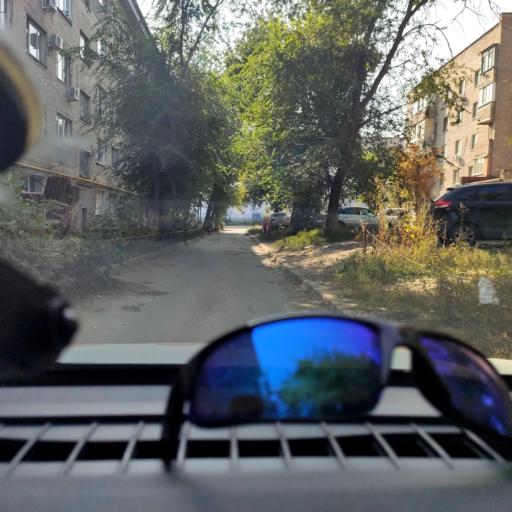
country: RU
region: Samara
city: Samara
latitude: 53.1863
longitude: 50.2000
